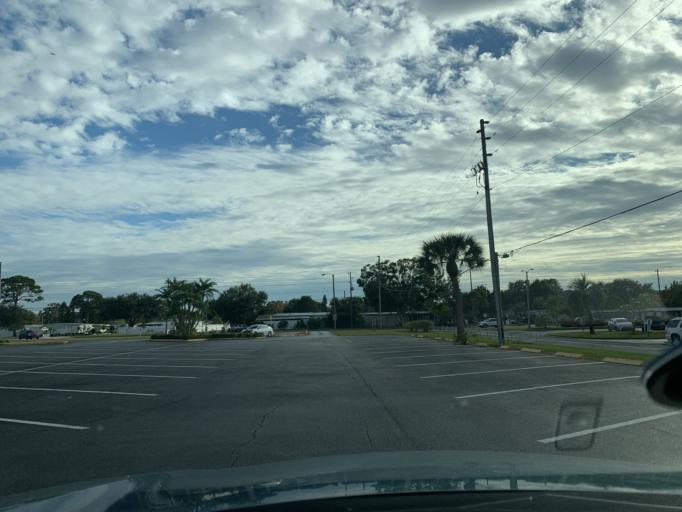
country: US
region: Florida
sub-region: Pinellas County
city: Kenneth City
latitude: 27.8219
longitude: -82.7480
